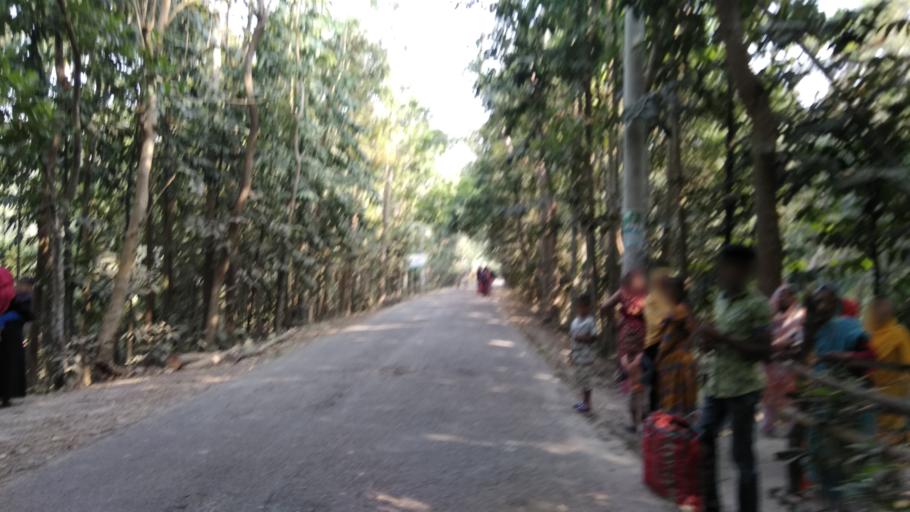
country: BD
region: Barisal
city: Mehendiganj
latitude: 22.9752
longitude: 90.4164
